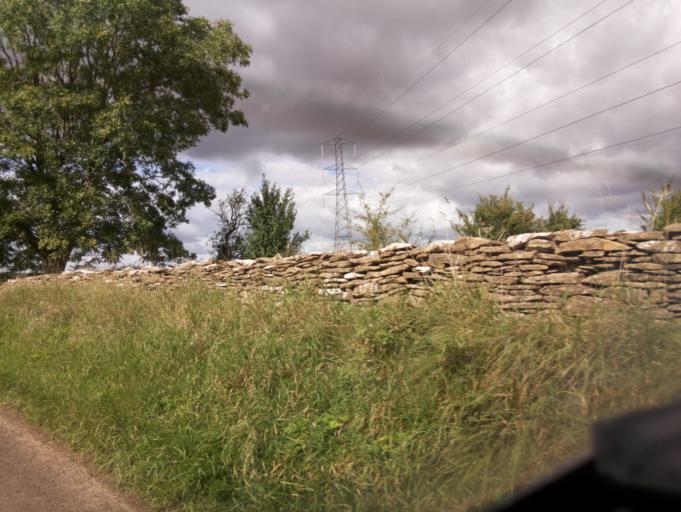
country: GB
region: England
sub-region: Wiltshire
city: Nettleton
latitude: 51.4931
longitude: -2.2892
